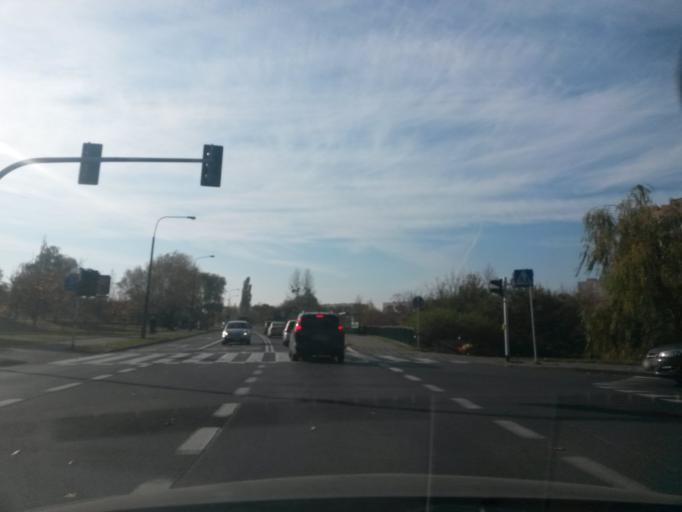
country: PL
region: Greater Poland Voivodeship
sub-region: Poznan
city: Poznan
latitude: 52.3811
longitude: 16.9572
